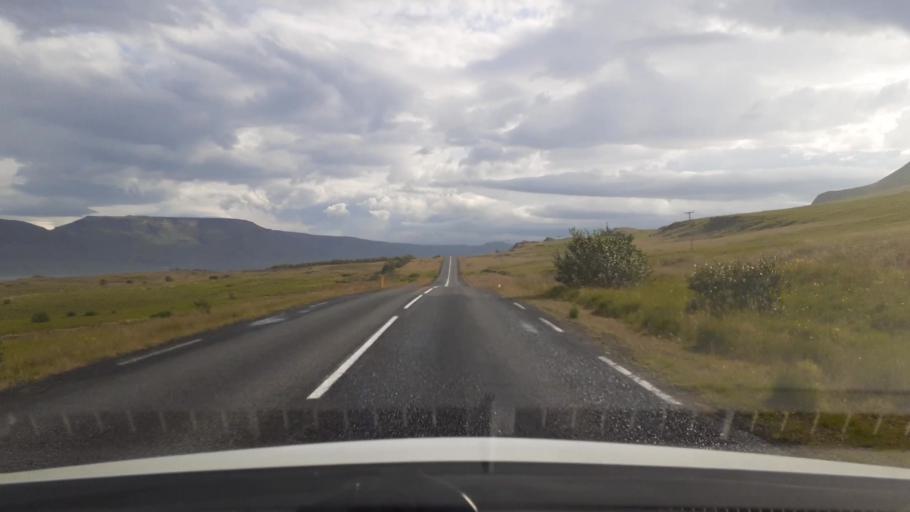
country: IS
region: Capital Region
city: Mosfellsbaer
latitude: 64.3623
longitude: -21.6179
